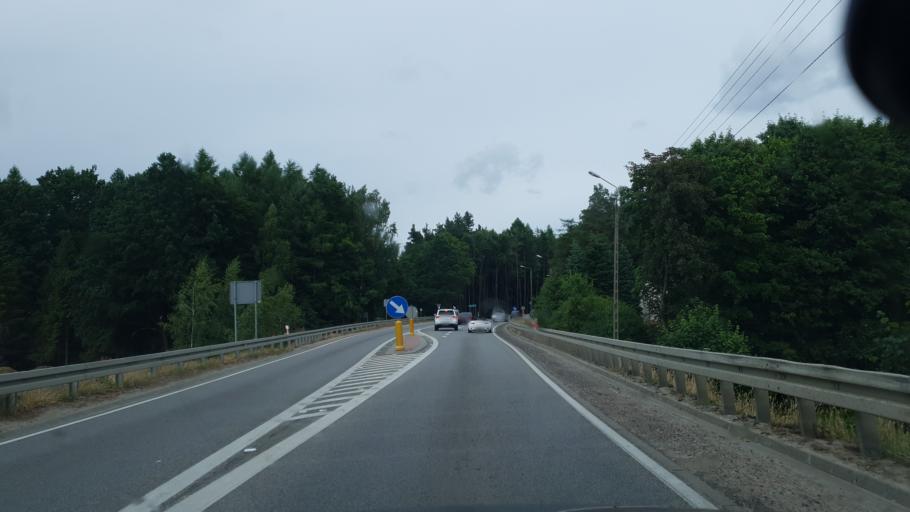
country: PL
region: Pomeranian Voivodeship
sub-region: Powiat kartuski
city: Chwaszczyno
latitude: 54.4303
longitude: 18.3912
